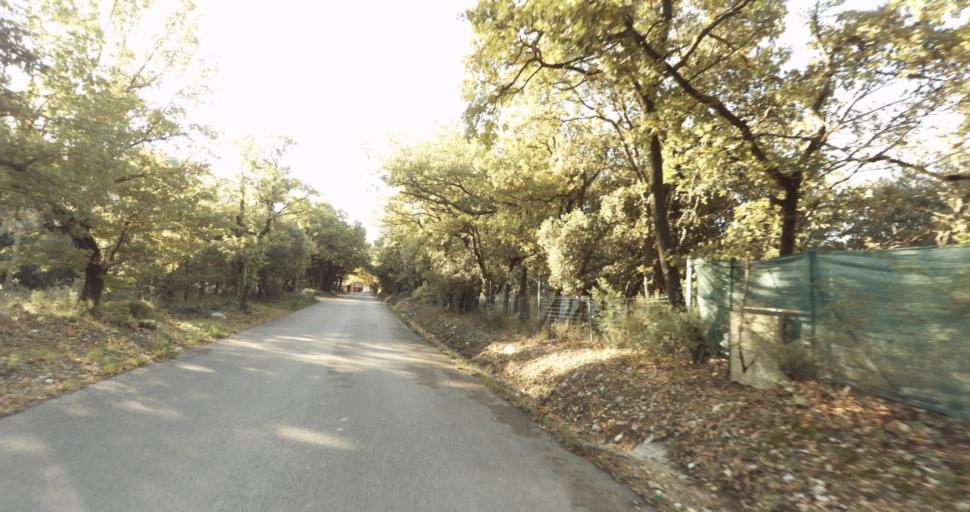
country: FR
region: Provence-Alpes-Cote d'Azur
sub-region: Departement des Bouches-du-Rhone
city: Venelles
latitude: 43.6019
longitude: 5.4743
